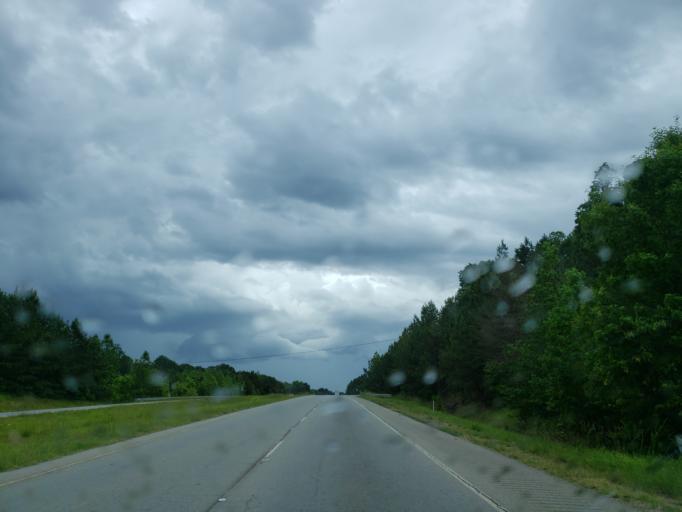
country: US
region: Georgia
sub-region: Haralson County
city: Buchanan
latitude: 33.9107
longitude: -85.2416
